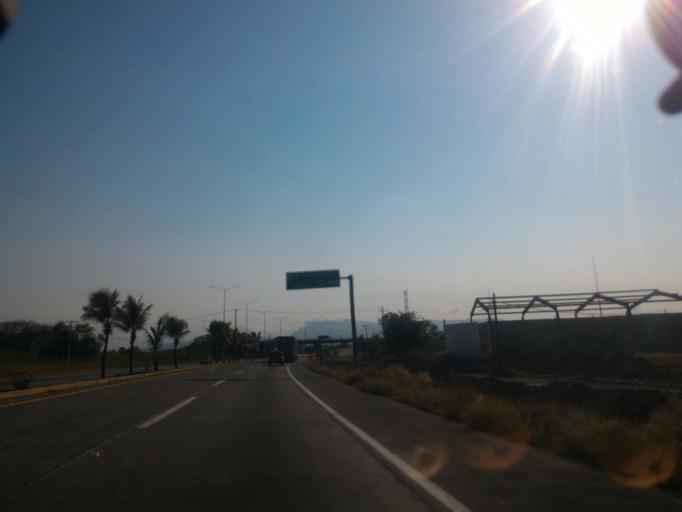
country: MX
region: Colima
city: Colima
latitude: 19.2588
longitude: -103.6839
